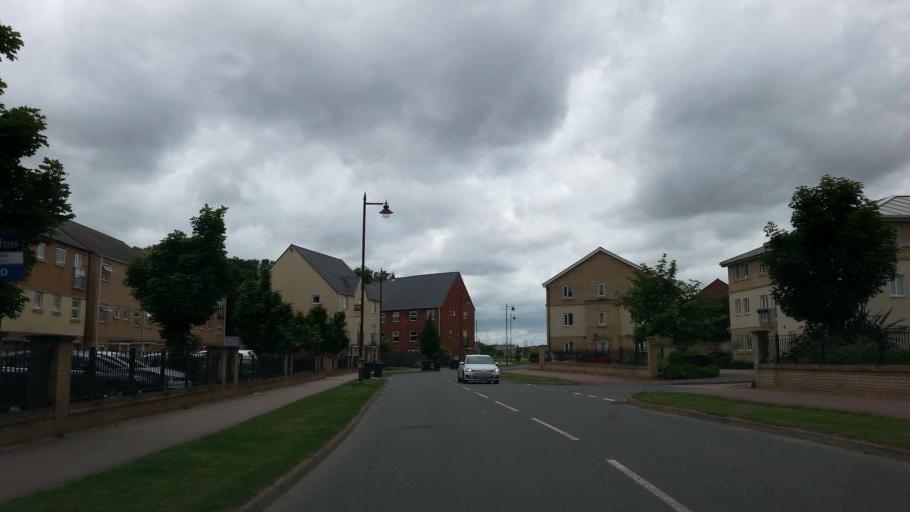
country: GB
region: England
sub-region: Cambridgeshire
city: Papworth Everard
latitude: 52.2180
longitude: -0.0565
